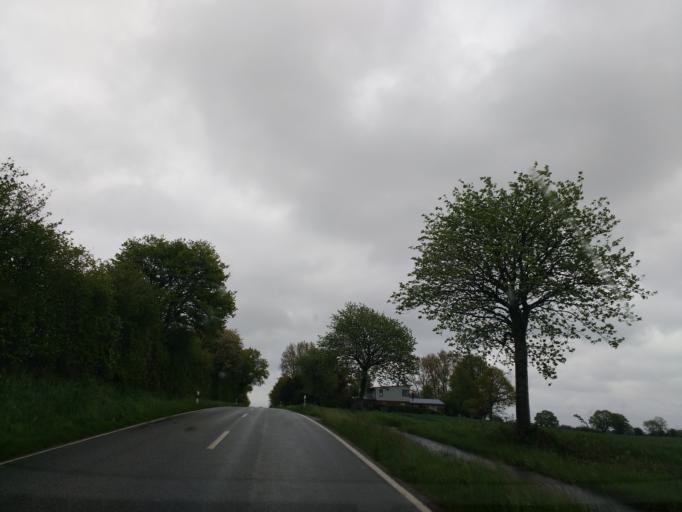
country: DE
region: Schleswig-Holstein
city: Waabs
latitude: 54.5292
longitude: 9.9714
